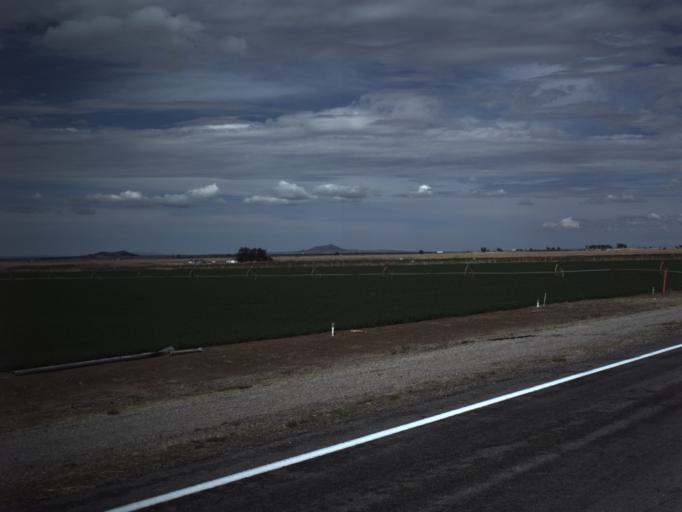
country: US
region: Utah
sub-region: Millard County
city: Fillmore
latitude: 38.8638
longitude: -112.4177
